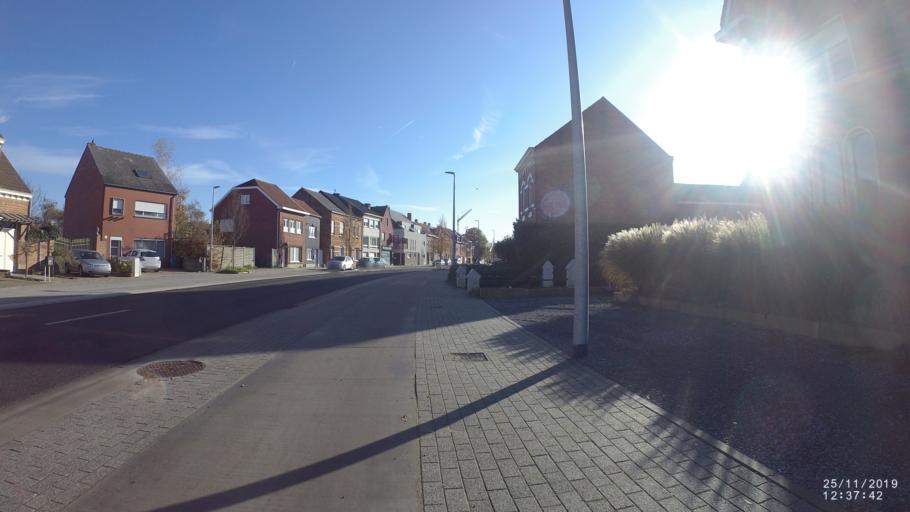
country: BE
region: Flanders
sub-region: Provincie Vlaams-Brabant
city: Aarschot
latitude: 50.9954
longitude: 4.8364
